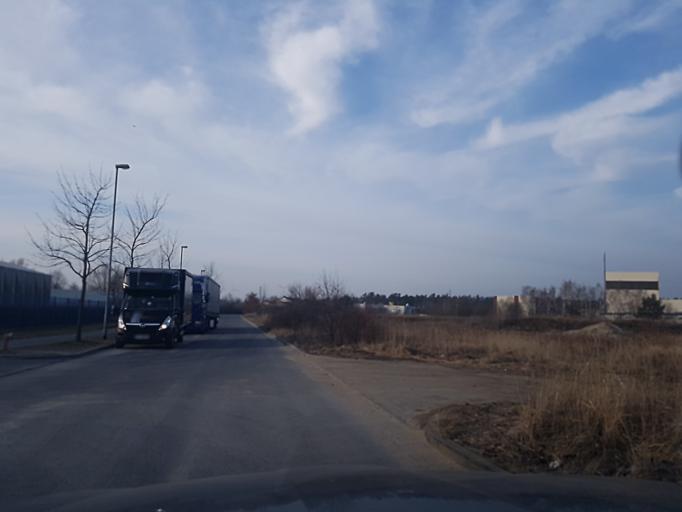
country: DE
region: Brandenburg
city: Finsterwalde
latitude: 51.6329
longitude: 13.7434
